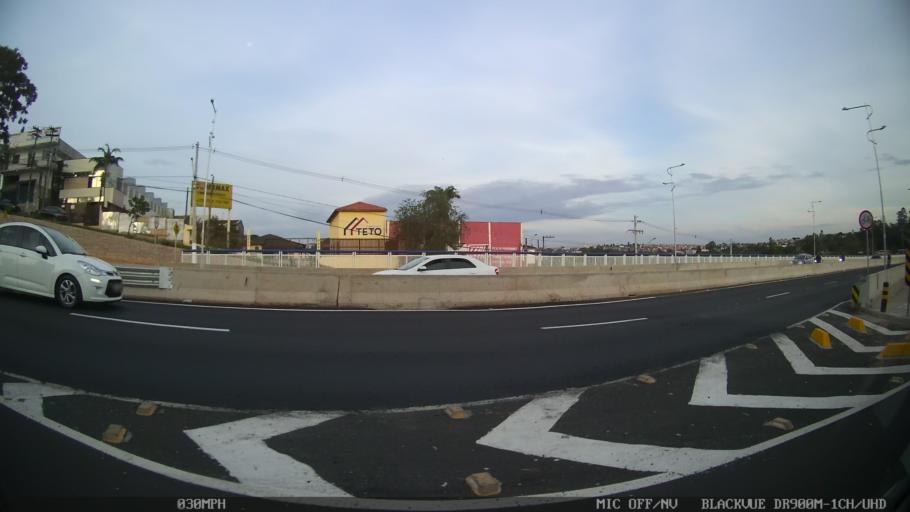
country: BR
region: Sao Paulo
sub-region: Limeira
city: Limeira
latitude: -22.5820
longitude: -47.4091
